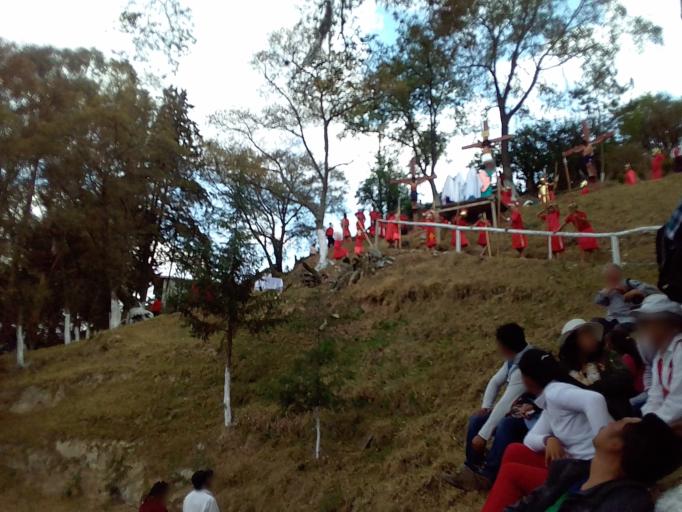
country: MX
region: Mexico
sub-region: Ixtlahuaca
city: San Lorenzo Toxico
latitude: 19.5371
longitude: -99.7657
